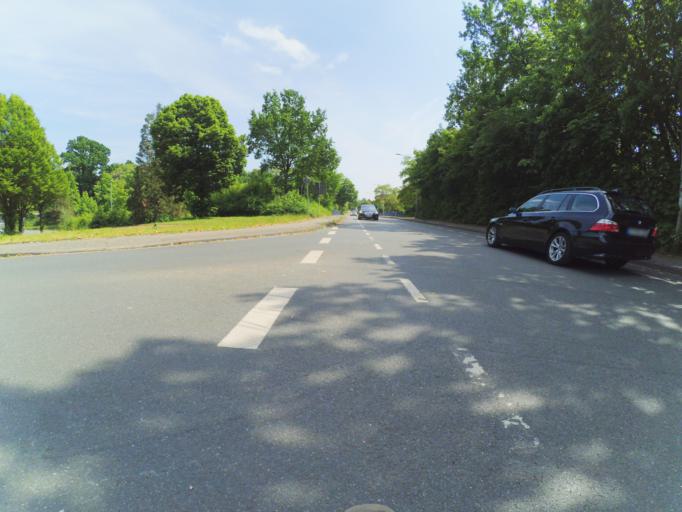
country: DE
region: North Rhine-Westphalia
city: Ibbenburen
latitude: 52.2787
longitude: 7.7194
